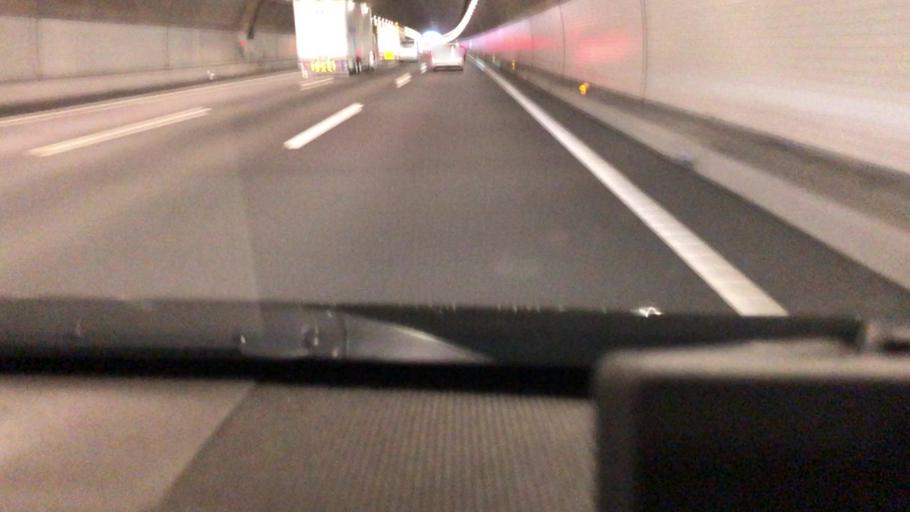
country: JP
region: Shizuoka
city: Shizuoka-shi
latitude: 35.0159
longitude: 138.3331
